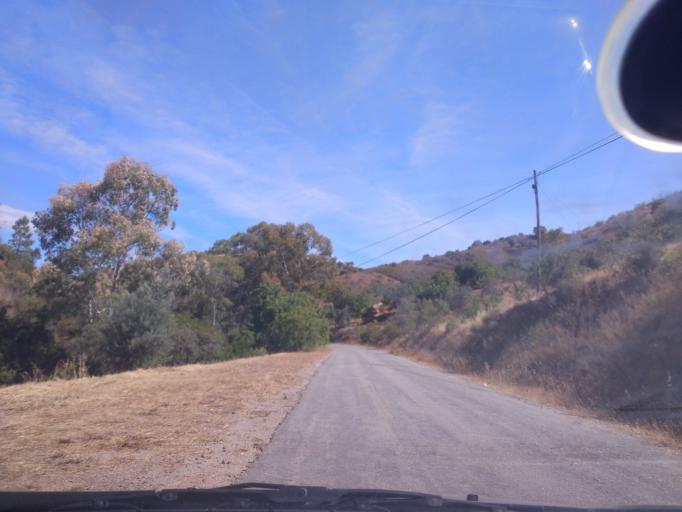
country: PT
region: Faro
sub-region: Olhao
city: Moncarapacho
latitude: 37.1612
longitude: -7.7985
